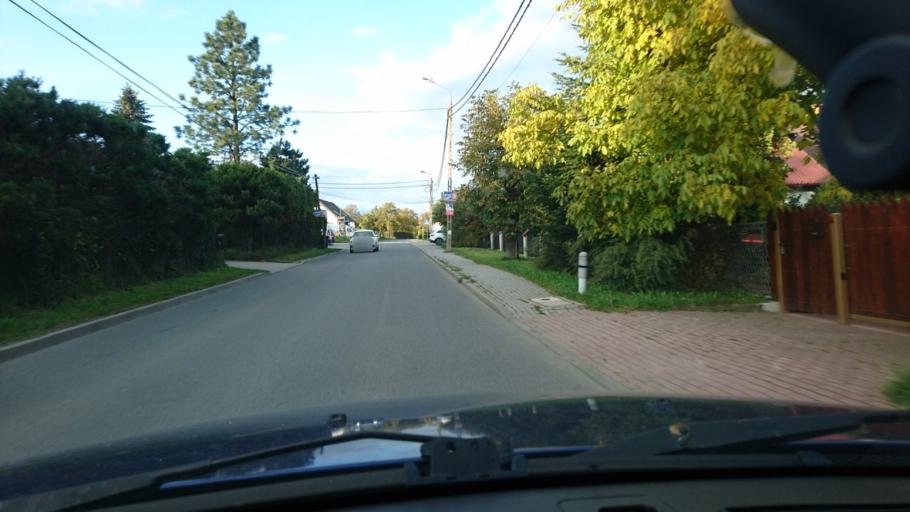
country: PL
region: Silesian Voivodeship
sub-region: Bielsko-Biala
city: Bielsko-Biala
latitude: 49.8053
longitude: 19.0173
